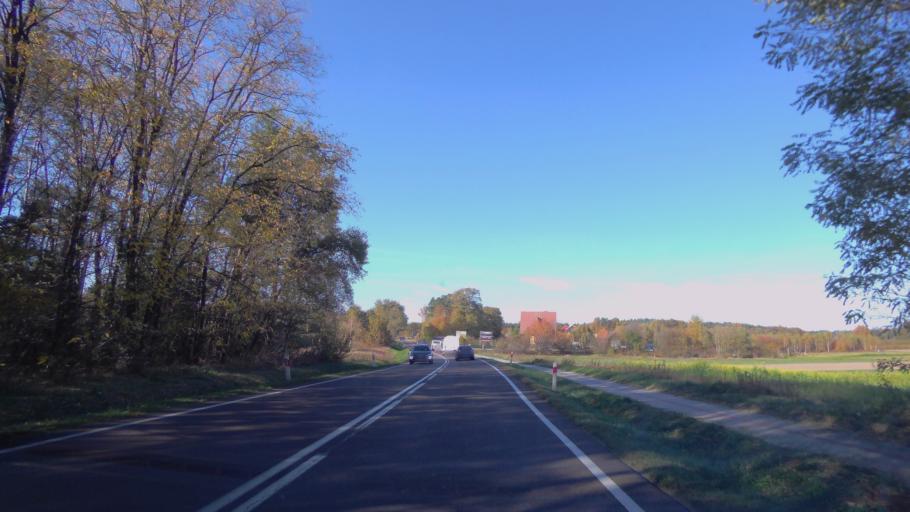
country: PL
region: Subcarpathian Voivodeship
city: Nowa Sarzyna
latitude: 50.3000
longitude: 22.3686
